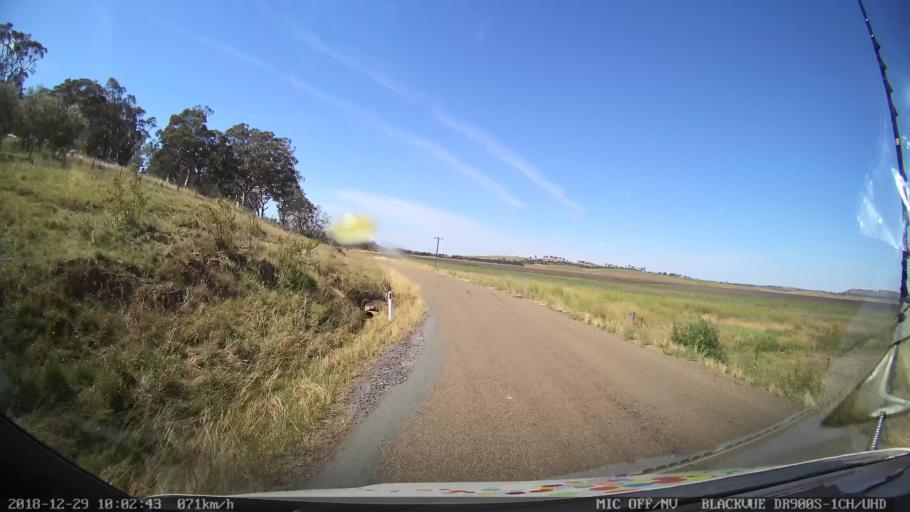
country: AU
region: New South Wales
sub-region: Goulburn Mulwaree
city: Goulburn
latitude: -34.8033
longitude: 149.4614
